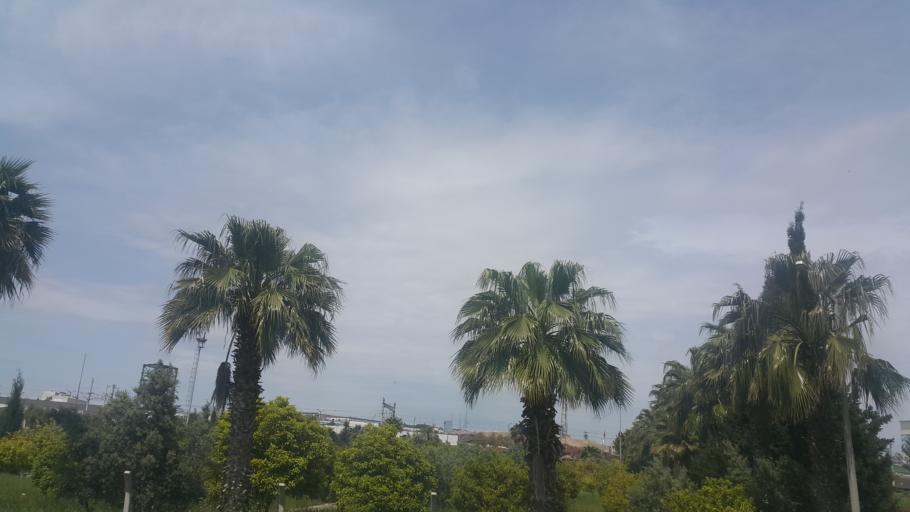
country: TR
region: Adana
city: Yakapinar
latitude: 36.9658
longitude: 35.6076
